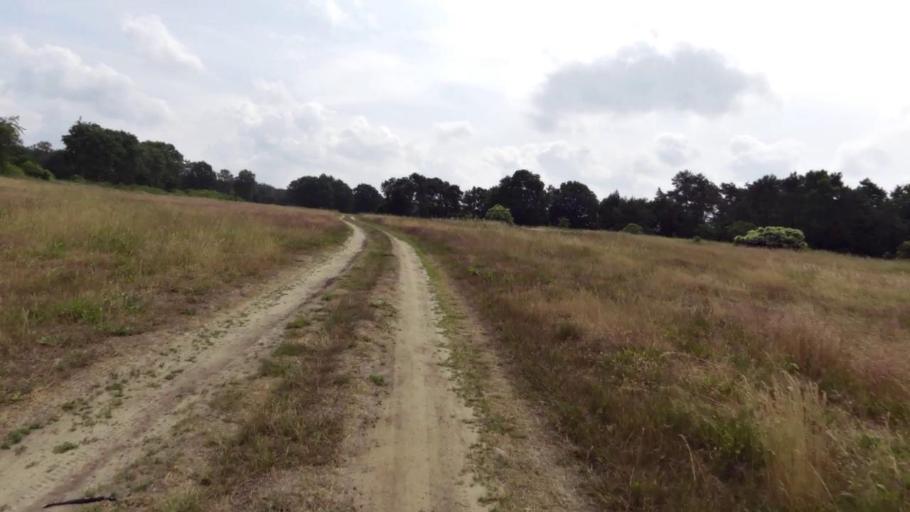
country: PL
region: West Pomeranian Voivodeship
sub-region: Powiat kamienski
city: Wolin
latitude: 53.7572
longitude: 14.6540
